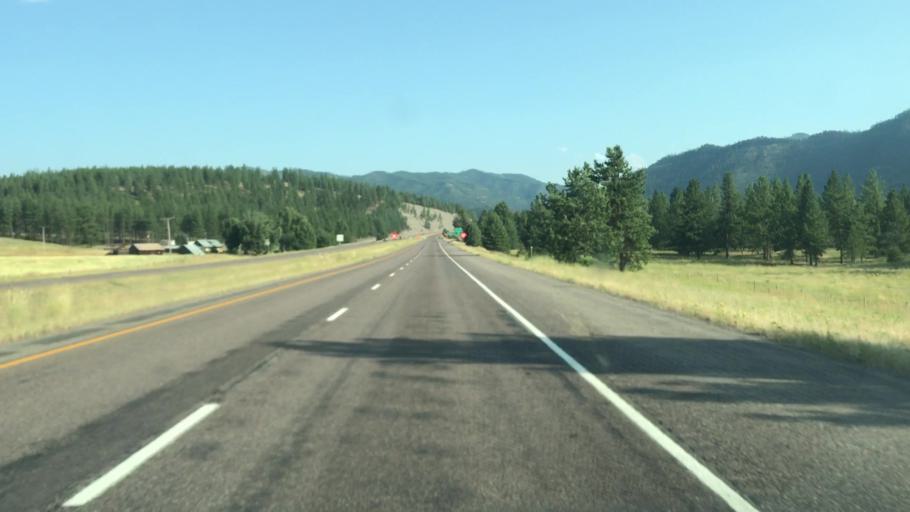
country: US
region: Montana
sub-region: Mineral County
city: Superior
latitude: 47.0315
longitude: -114.7432
